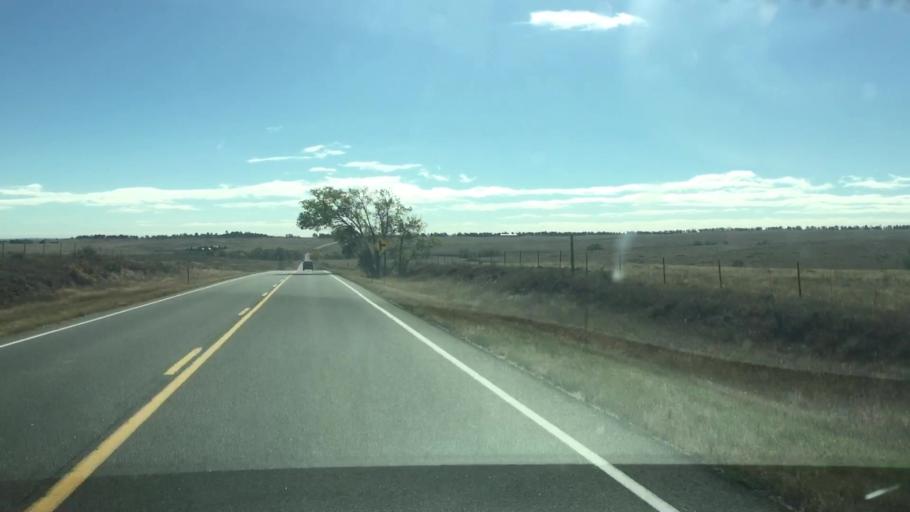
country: US
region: Colorado
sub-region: Elbert County
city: Kiowa
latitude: 39.3262
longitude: -104.3967
